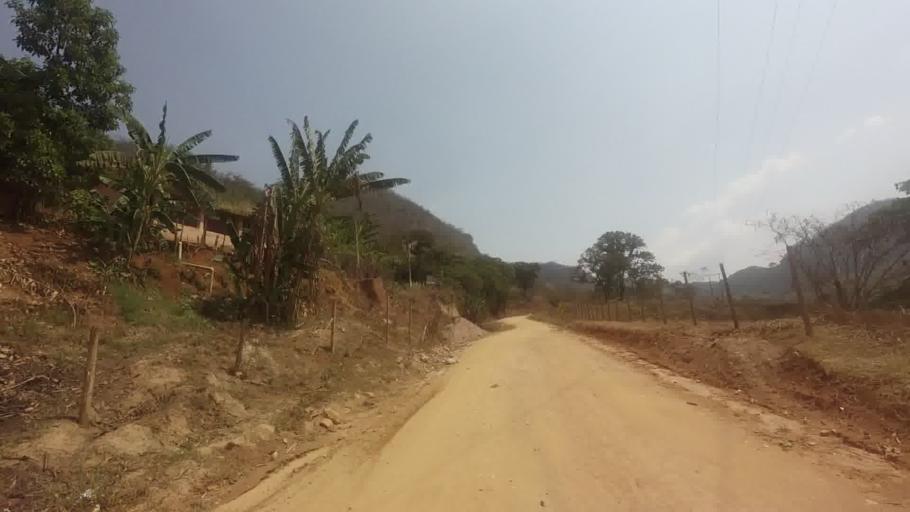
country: BR
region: Espirito Santo
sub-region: Mimoso Do Sul
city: Mimoso do Sul
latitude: -20.9468
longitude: -41.3758
